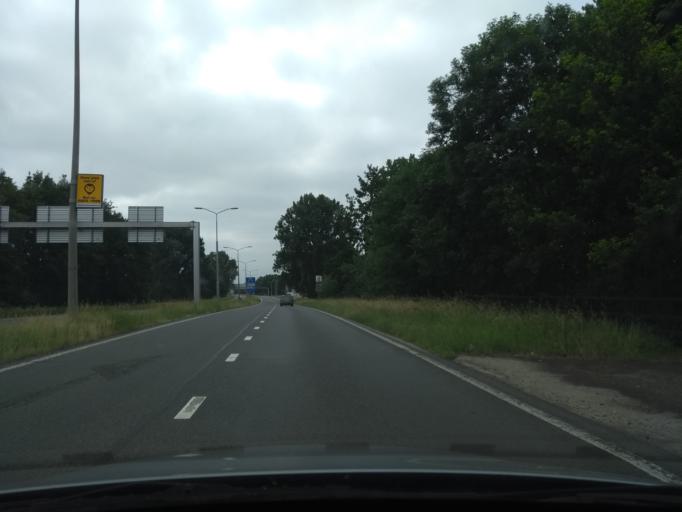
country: NL
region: Overijssel
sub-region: Gemeente Wierden
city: Wierden
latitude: 52.3552
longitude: 6.6247
